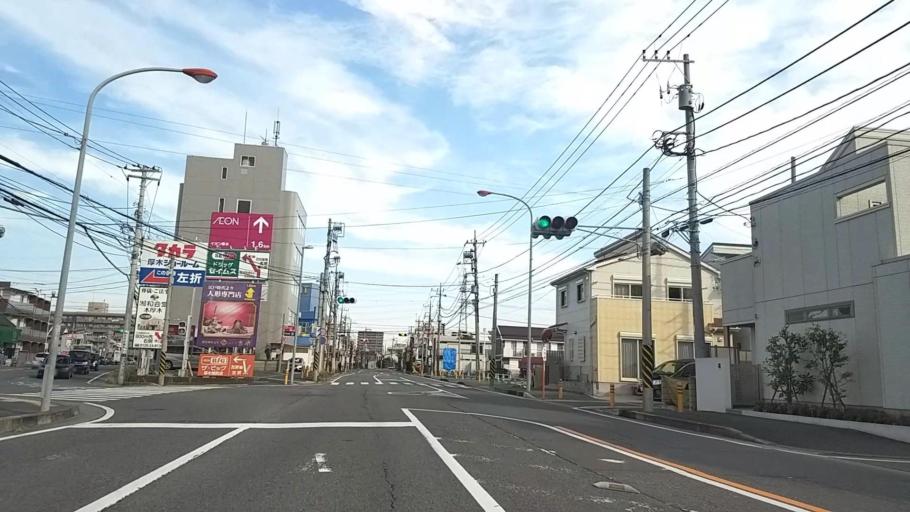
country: JP
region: Kanagawa
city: Atsugi
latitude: 35.4288
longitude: 139.3658
